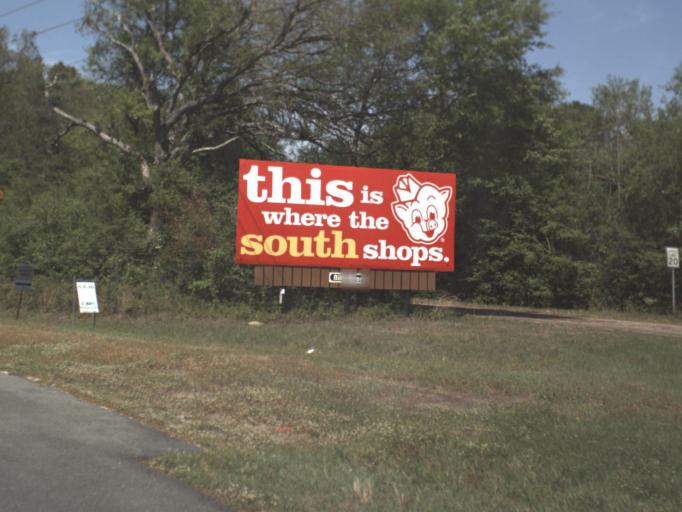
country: US
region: Florida
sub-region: Santa Rosa County
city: East Milton
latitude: 30.6250
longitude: -87.0166
